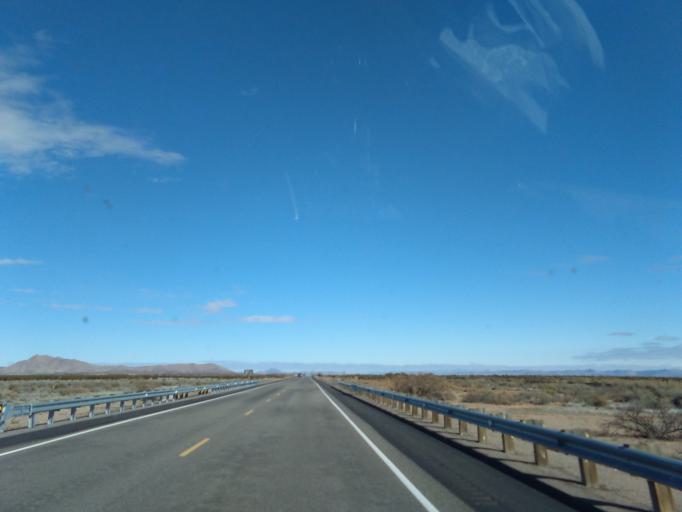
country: US
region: New Mexico
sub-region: Luna County
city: Deming
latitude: 32.3189
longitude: -107.6791
